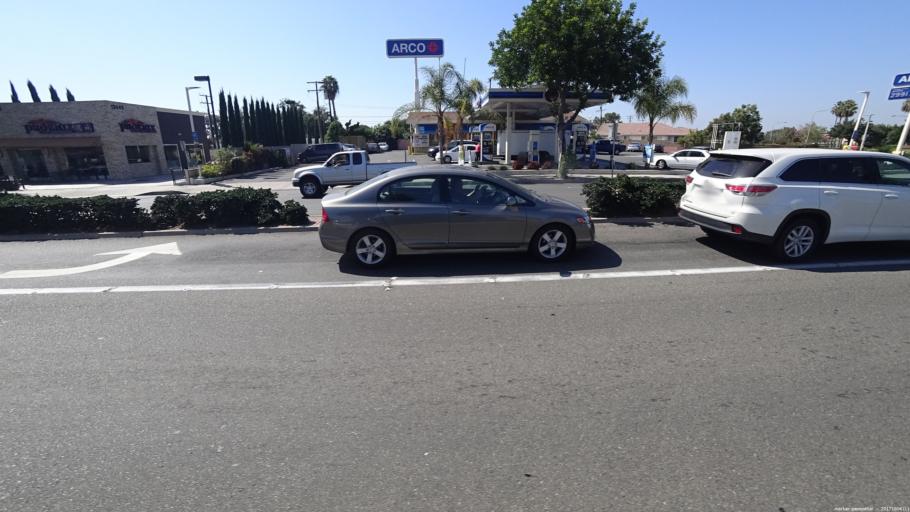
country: US
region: California
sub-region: Orange County
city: Garden Grove
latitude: 33.7688
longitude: -117.9377
